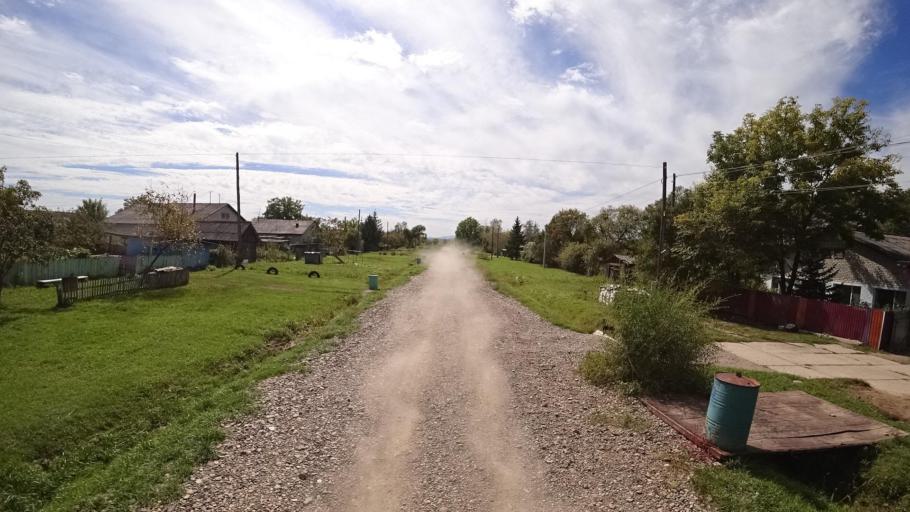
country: RU
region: Primorskiy
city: Yakovlevka
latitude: 44.6425
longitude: 133.6015
